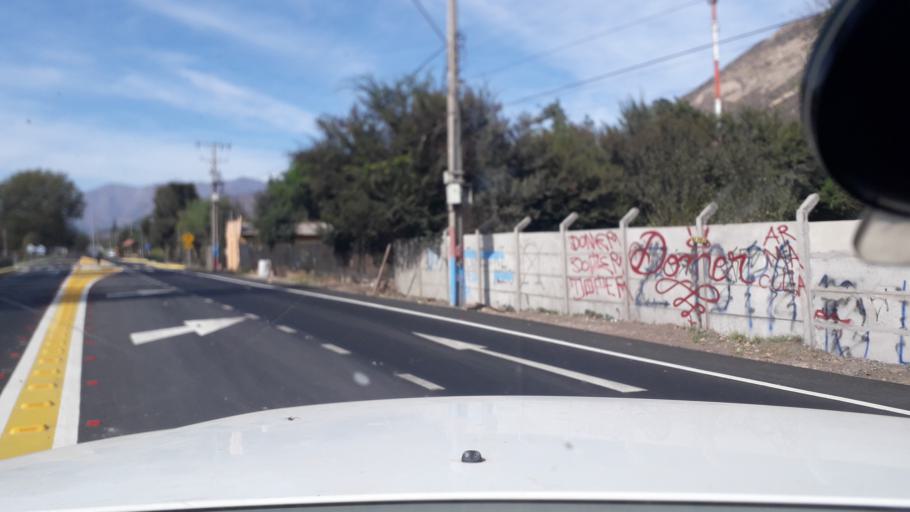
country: CL
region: Valparaiso
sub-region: Provincia de San Felipe
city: Llaillay
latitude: -32.8033
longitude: -70.9048
